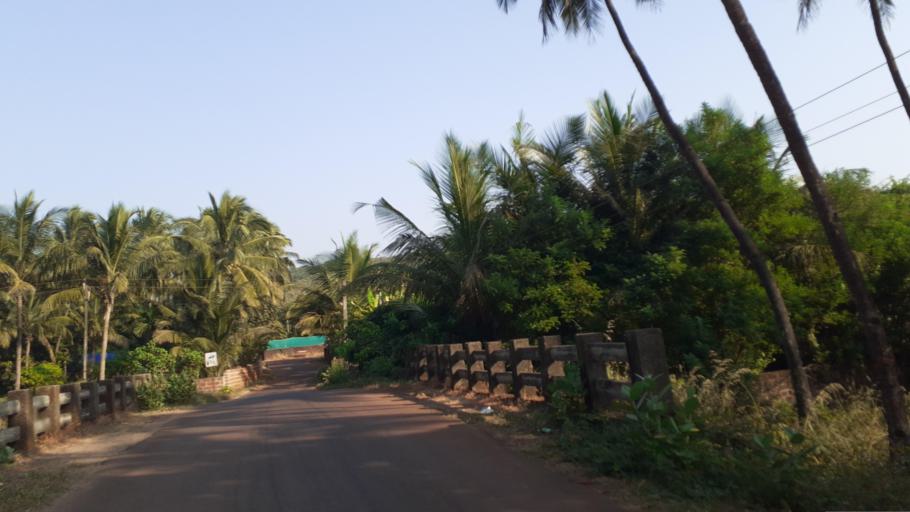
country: IN
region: Maharashtra
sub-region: Ratnagiri
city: Ratnagiri
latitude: 17.2125
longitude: 73.2481
